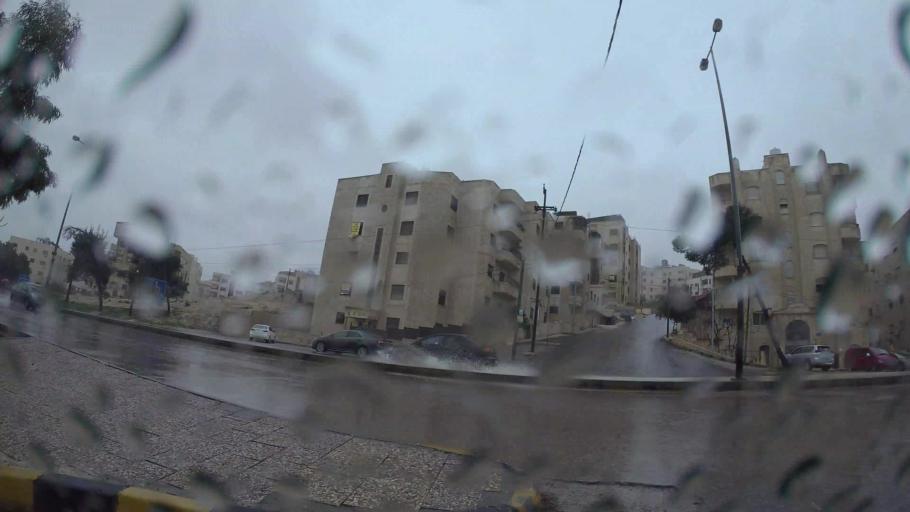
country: JO
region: Amman
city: Al Jubayhah
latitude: 32.0296
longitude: 35.8888
